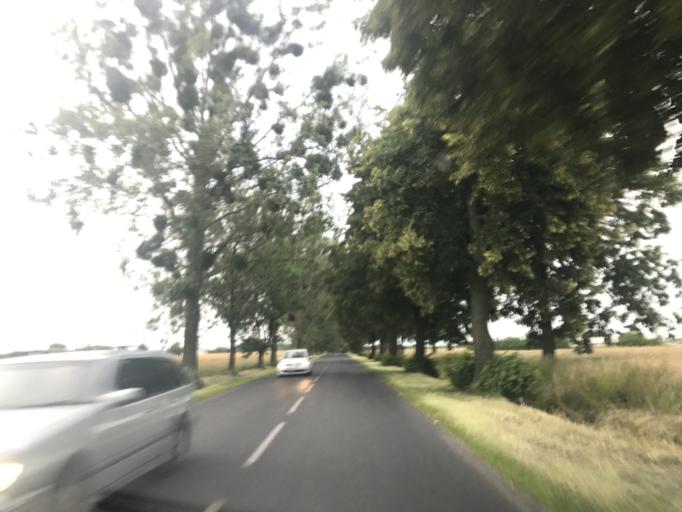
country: PL
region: Kujawsko-Pomorskie
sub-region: Powiat rypinski
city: Rogowo
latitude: 53.0059
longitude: 19.3446
